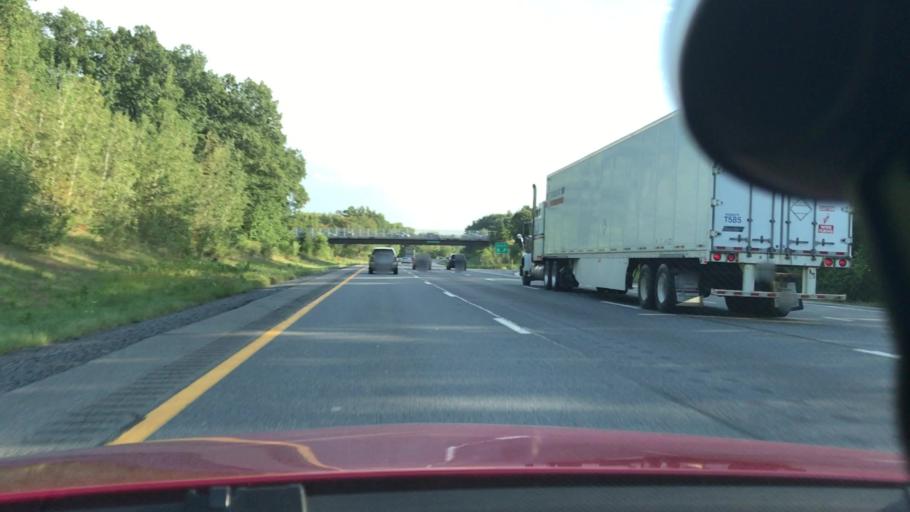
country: US
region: New York
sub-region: Albany County
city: Cohoes
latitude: 42.8219
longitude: -73.7685
